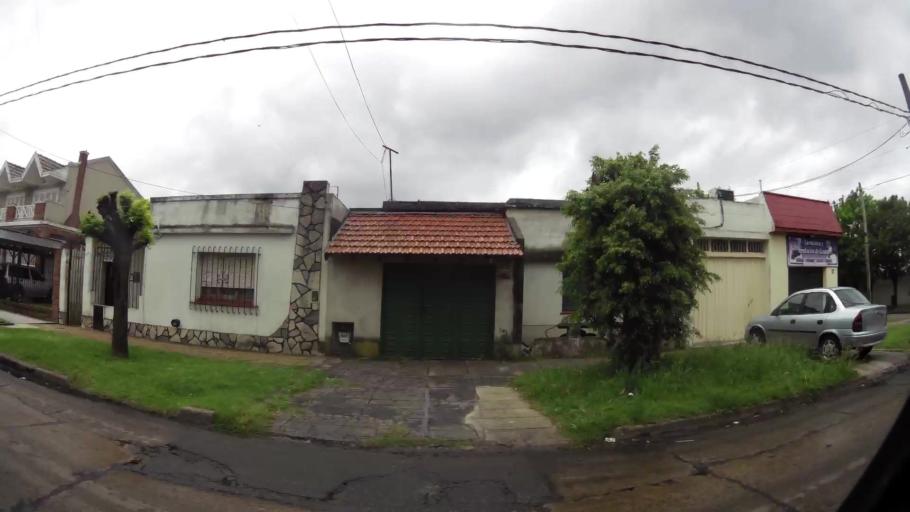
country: AR
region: Buenos Aires
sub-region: Partido de Lomas de Zamora
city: Lomas de Zamora
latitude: -34.7515
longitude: -58.3831
